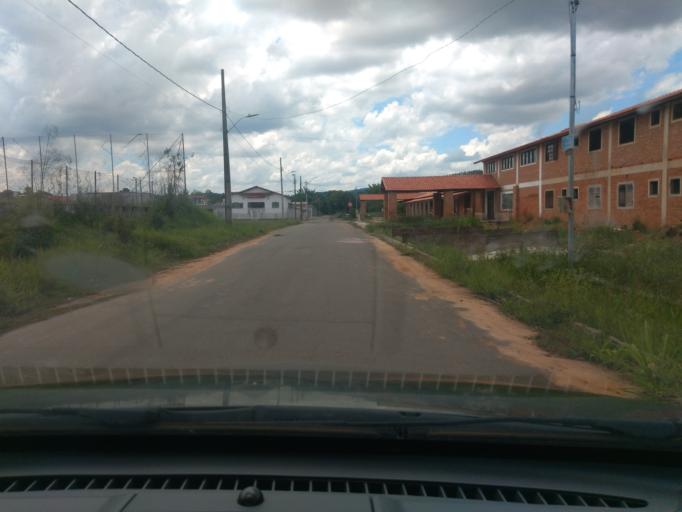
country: BR
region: Minas Gerais
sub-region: Tres Coracoes
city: Tres Coracoes
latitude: -21.6720
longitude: -45.2652
